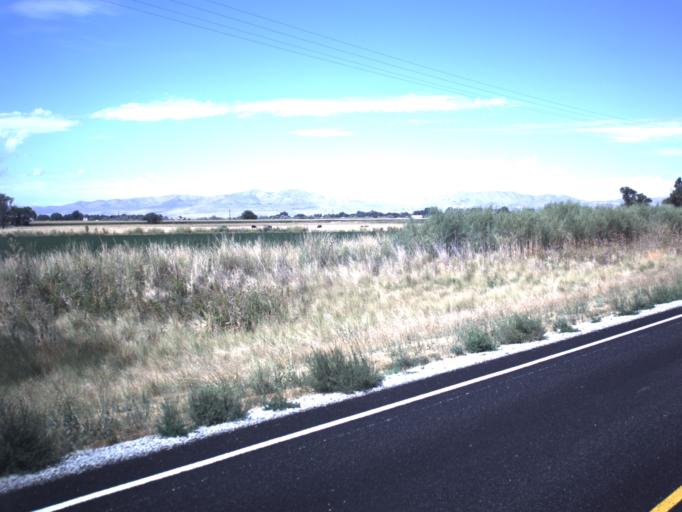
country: US
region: Utah
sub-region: Box Elder County
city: Elwood
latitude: 41.6455
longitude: -112.1327
